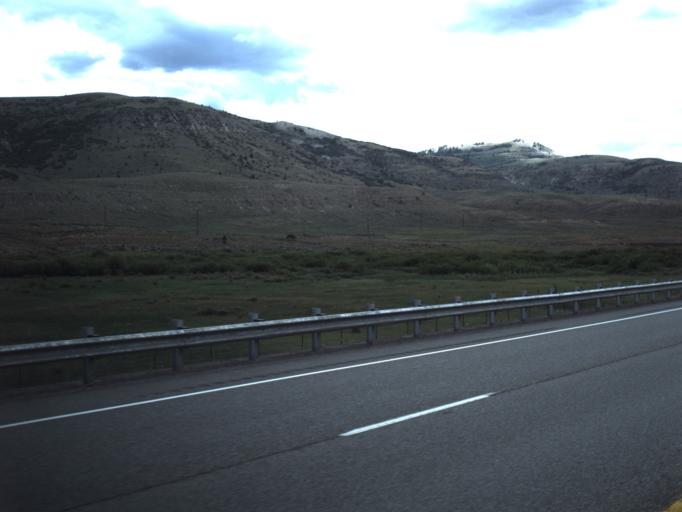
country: US
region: Utah
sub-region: Carbon County
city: Helper
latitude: 39.8808
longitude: -111.0438
